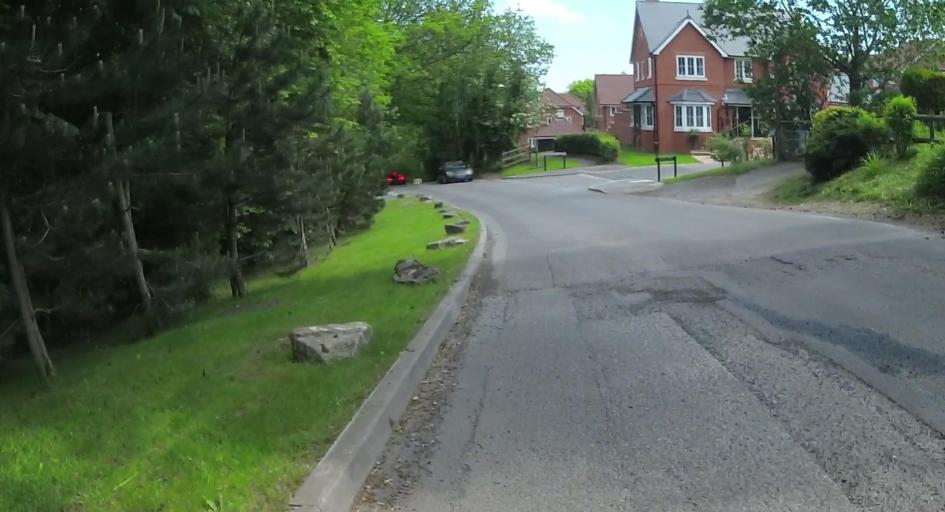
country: GB
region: England
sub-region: Surrey
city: Farnham
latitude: 51.1884
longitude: -0.8040
